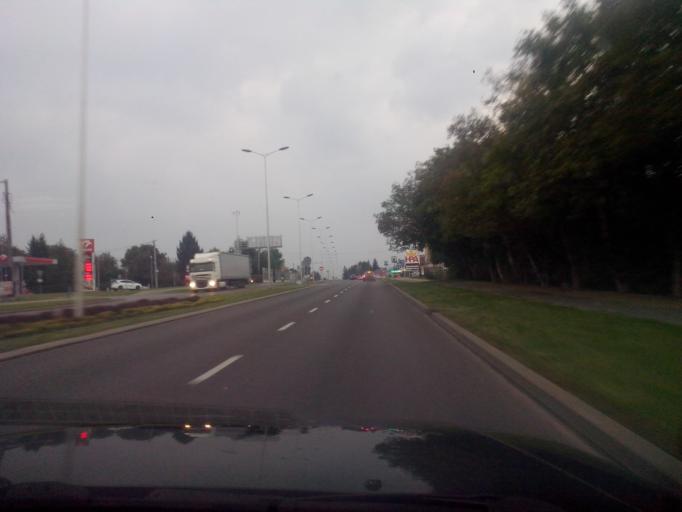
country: PL
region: Subcarpathian Voivodeship
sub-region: Rzeszow
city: Rzeszow
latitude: 50.0147
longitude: 21.9718
